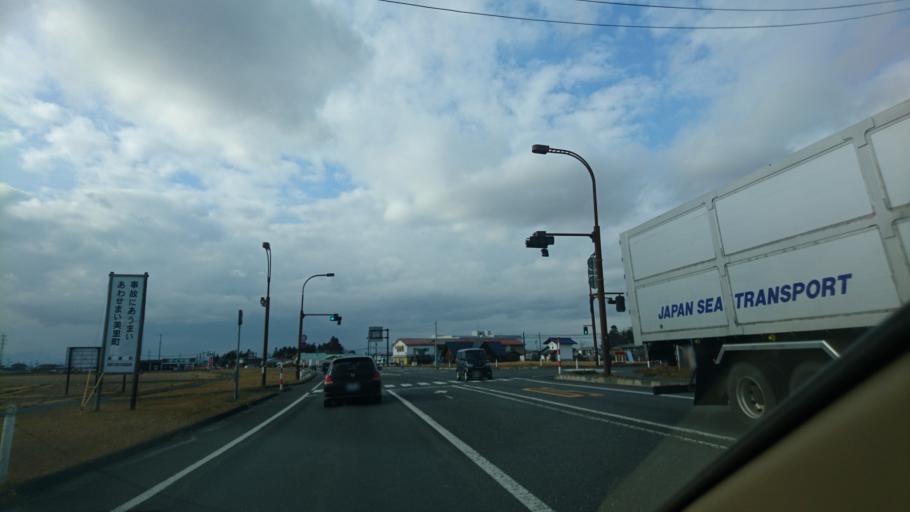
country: JP
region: Miyagi
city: Kogota
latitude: 38.5593
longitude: 141.0345
